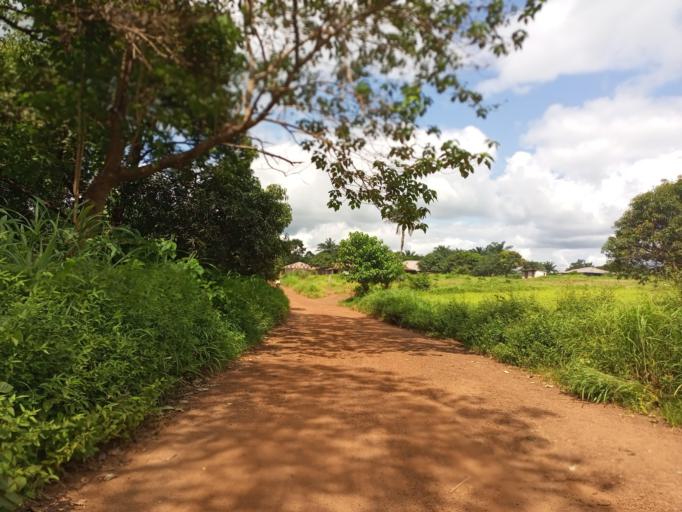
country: SL
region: Northern Province
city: Kamakwie
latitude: 9.5032
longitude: -12.2354
